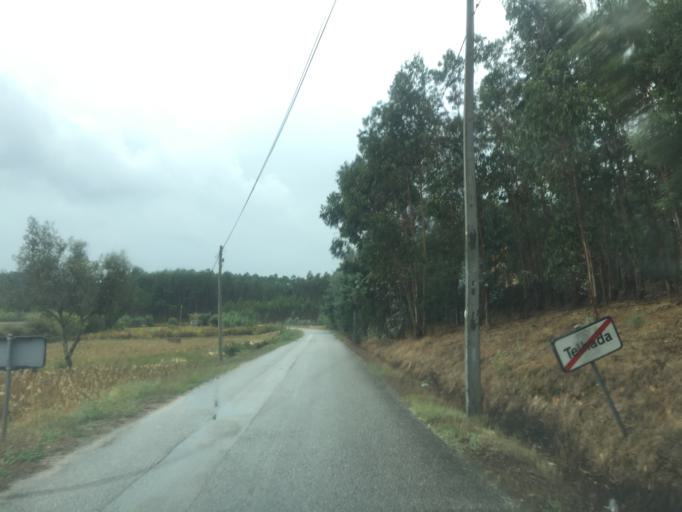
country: PT
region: Leiria
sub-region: Pombal
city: Lourical
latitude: 40.0575
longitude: -8.7723
